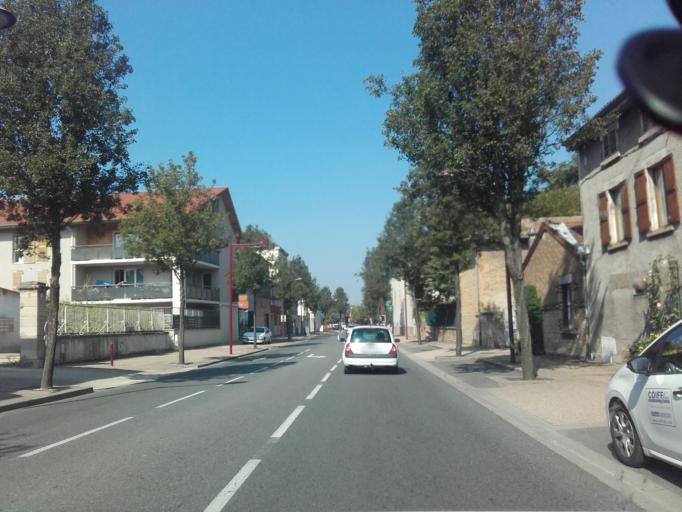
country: FR
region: Bourgogne
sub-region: Departement de Saone-et-Loire
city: Creches-sur-Saone
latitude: 46.2444
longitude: 4.7873
